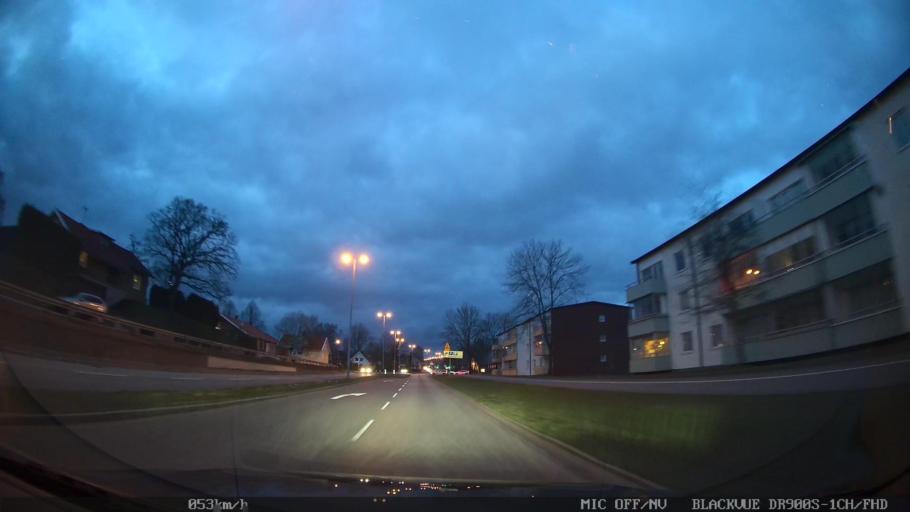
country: SE
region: Skane
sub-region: Hassleholms Kommun
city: Hassleholm
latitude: 56.1600
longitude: 13.7557
